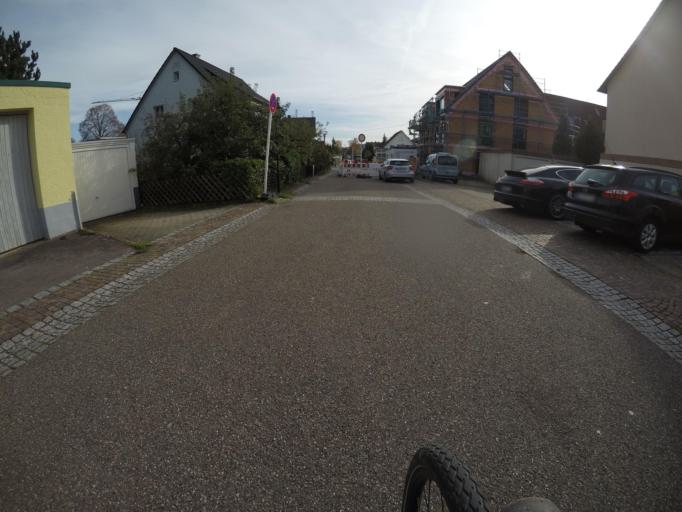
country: DE
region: Baden-Wuerttemberg
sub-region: Regierungsbezirk Stuttgart
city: Weil der Stadt
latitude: 48.7677
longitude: 8.8558
